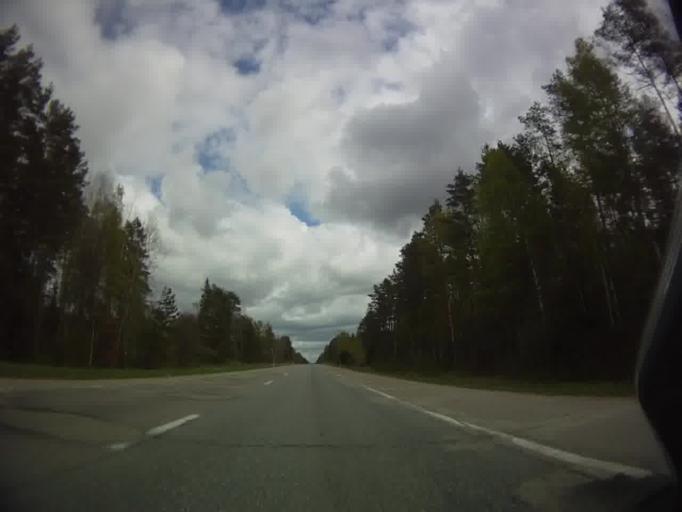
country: LV
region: Incukalns
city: Vangazi
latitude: 57.0982
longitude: 24.5797
